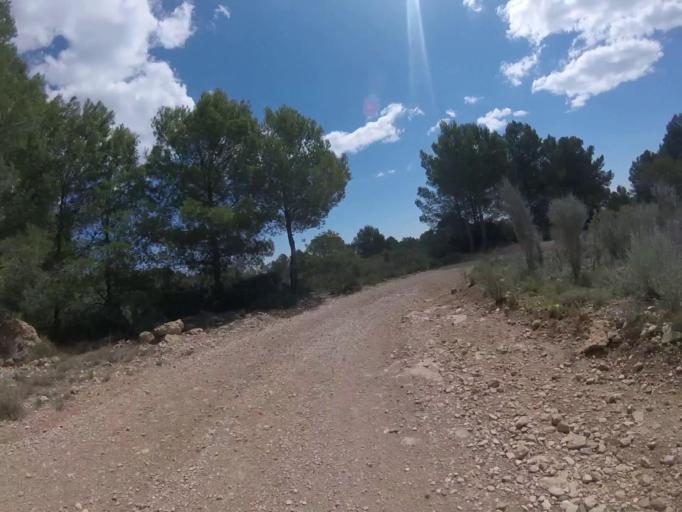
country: ES
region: Valencia
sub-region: Provincia de Castello
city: Alcoceber
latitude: 40.2861
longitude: 0.3225
